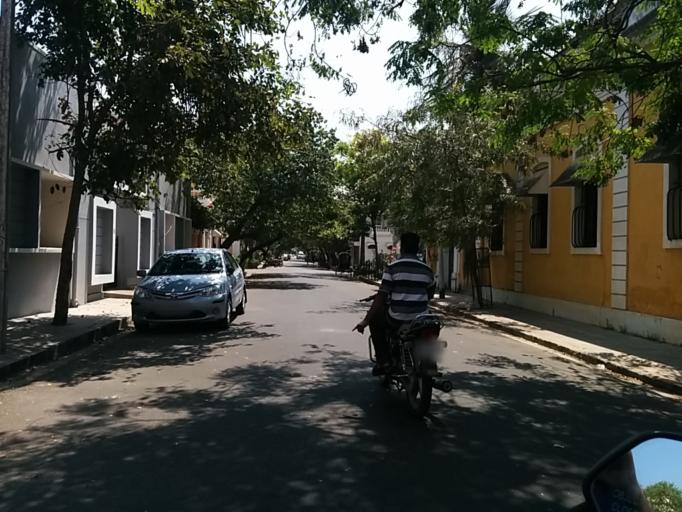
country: IN
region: Pondicherry
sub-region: Puducherry
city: Puducherry
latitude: 11.9279
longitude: 79.8342
